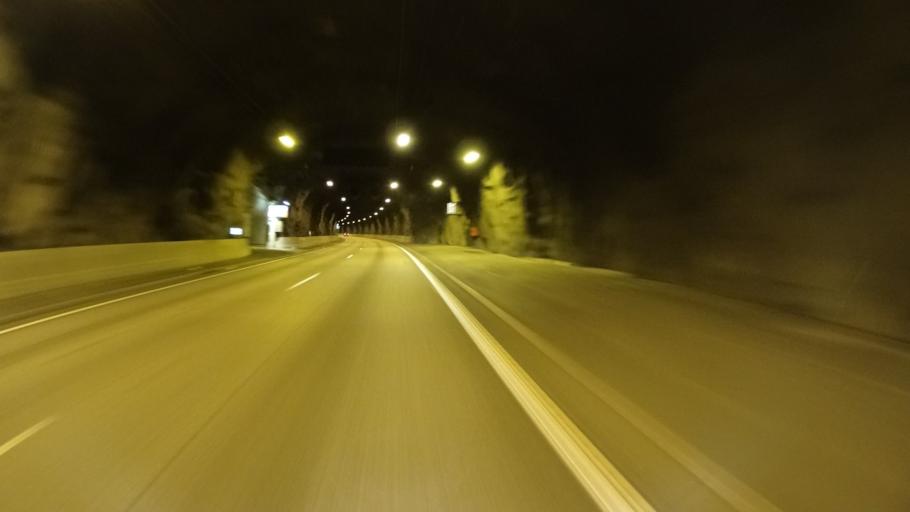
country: FI
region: Uusimaa
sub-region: Helsinki
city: Vantaa
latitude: 60.2383
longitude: 25.1595
